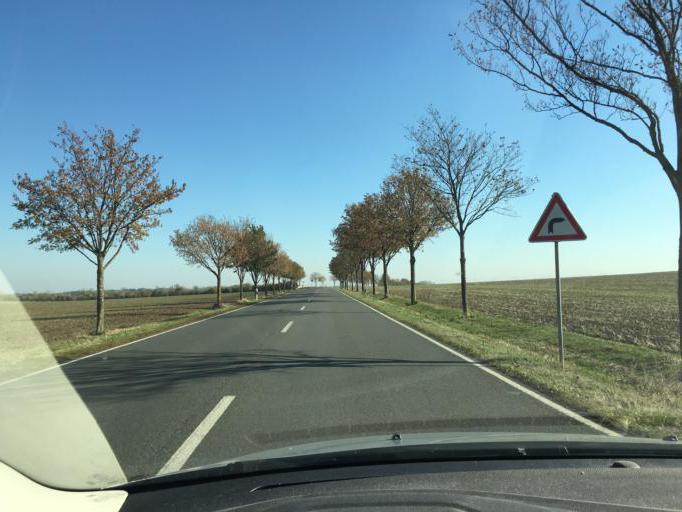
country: DE
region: Saxony-Anhalt
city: Wanzleben
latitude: 52.0345
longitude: 11.4706
